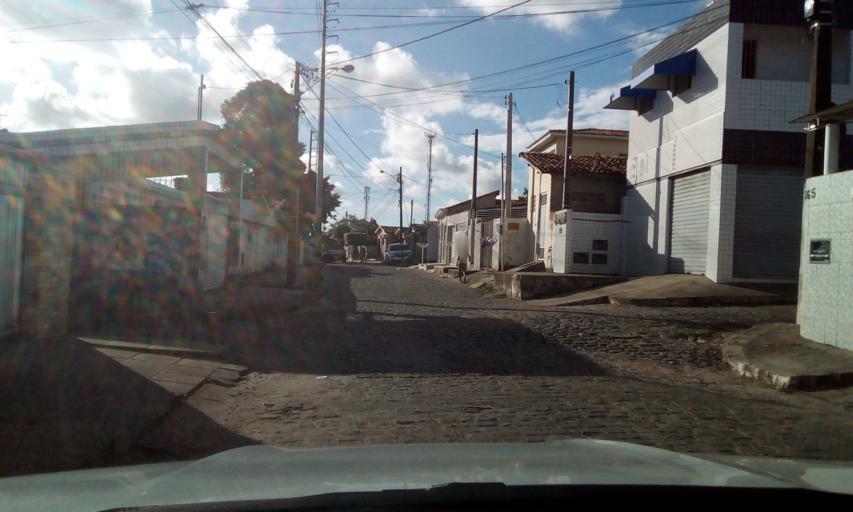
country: BR
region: Paraiba
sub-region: Joao Pessoa
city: Joao Pessoa
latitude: -7.1120
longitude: -34.8676
